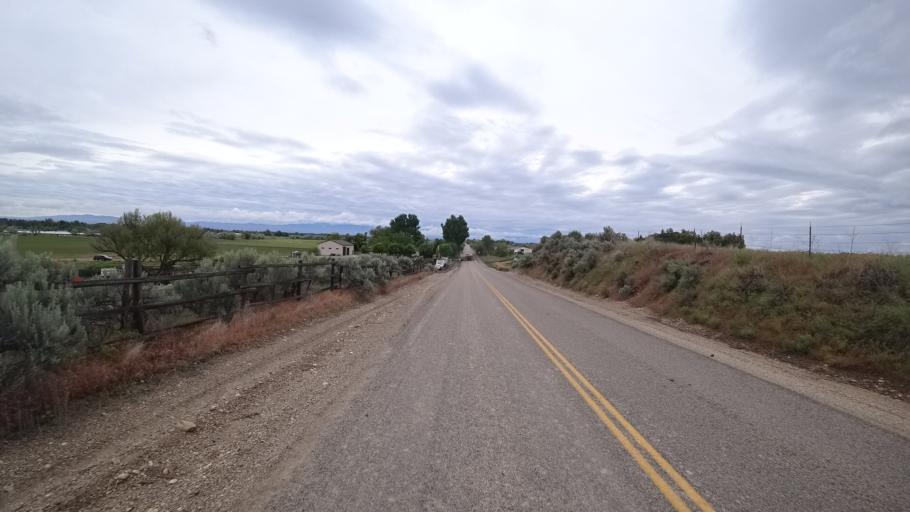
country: US
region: Idaho
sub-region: Ada County
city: Star
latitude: 43.6704
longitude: -116.5069
